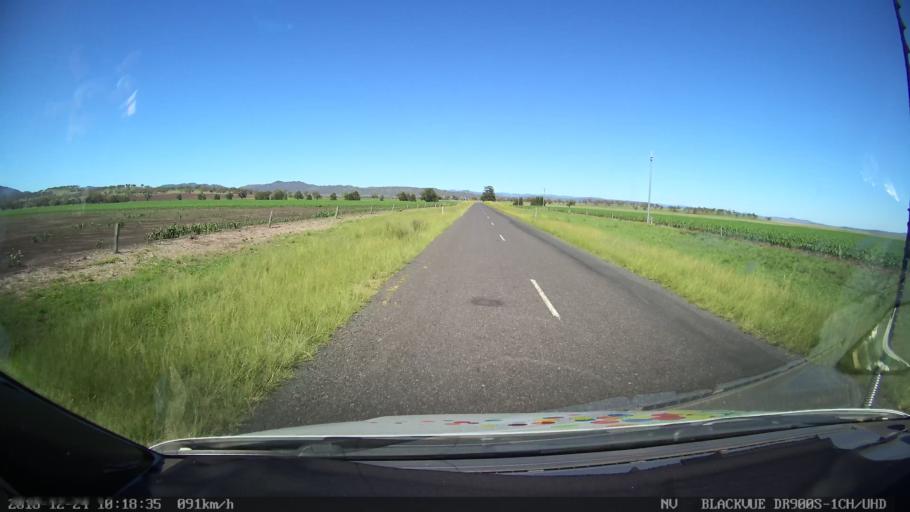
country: AU
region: New South Wales
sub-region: Liverpool Plains
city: Quirindi
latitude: -31.7243
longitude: 150.5741
